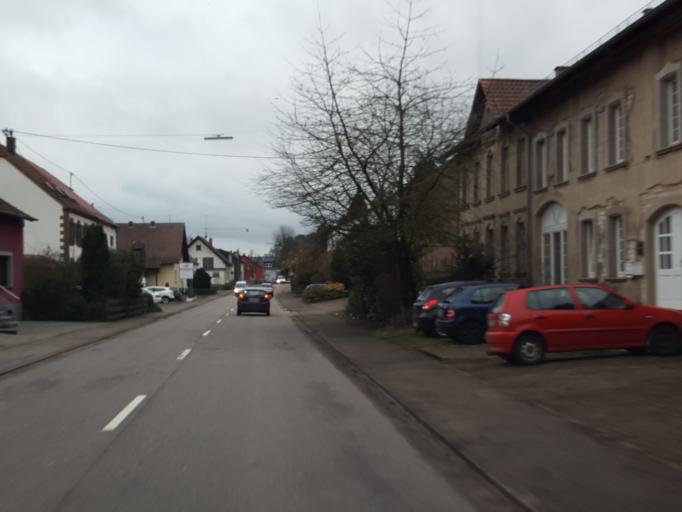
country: DE
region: Saarland
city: Beckingen
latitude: 49.4460
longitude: 6.7392
